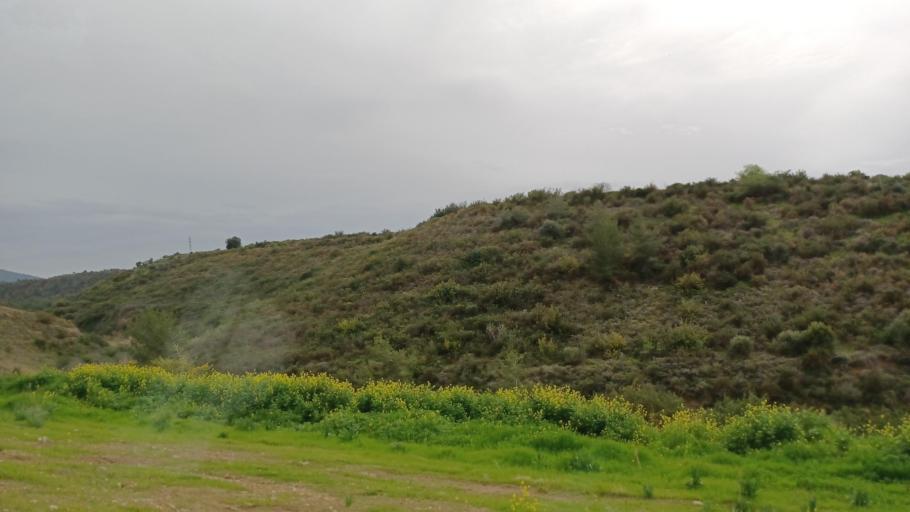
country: CY
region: Pafos
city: Polis
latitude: 35.0511
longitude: 32.4706
